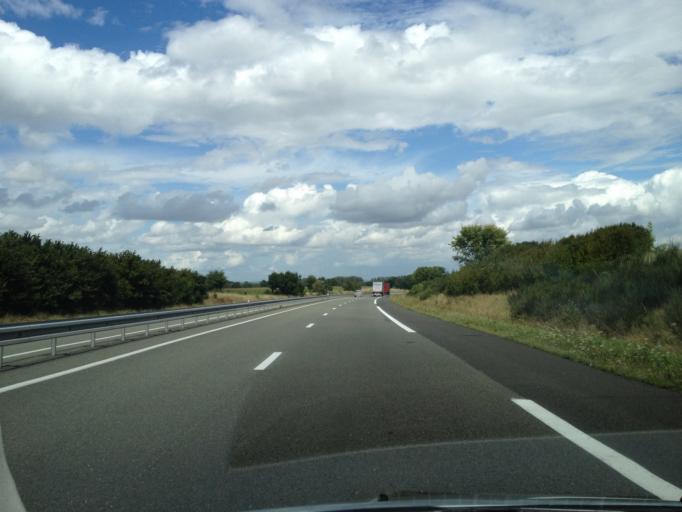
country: FR
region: Pays de la Loire
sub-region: Departement de la Sarthe
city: Sainte-Jamme-sur-Sarthe
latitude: 48.1696
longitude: 0.1445
